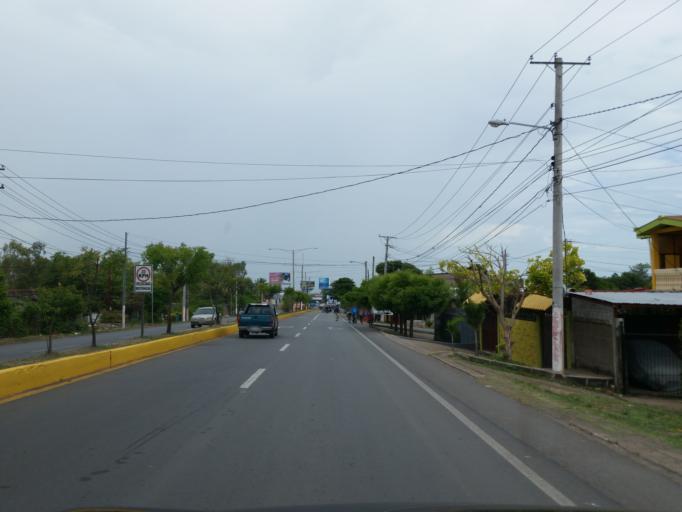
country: NI
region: Granada
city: Granada
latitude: 11.9359
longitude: -85.9705
